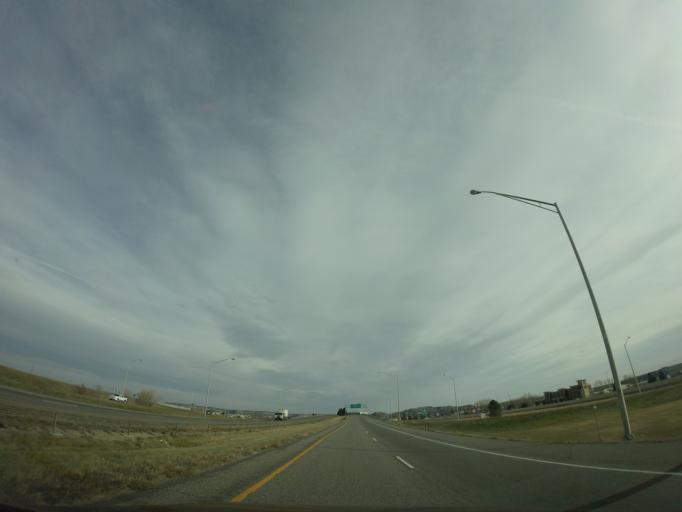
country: US
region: Montana
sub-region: Yellowstone County
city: Billings
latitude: 45.7493
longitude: -108.5621
